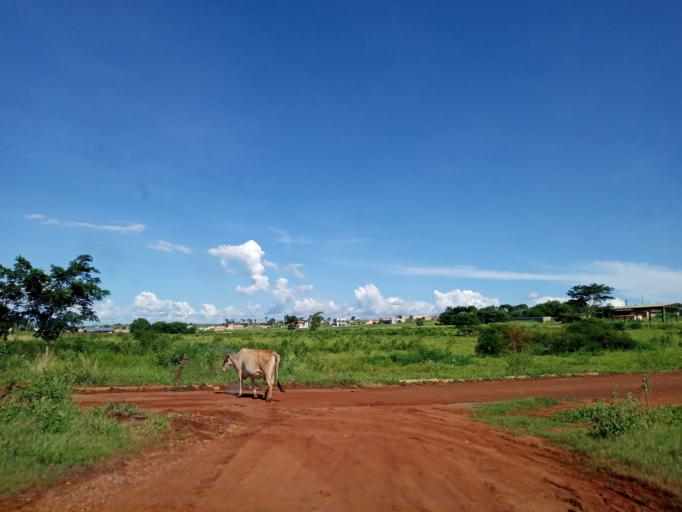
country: BR
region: Goias
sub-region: Itumbiara
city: Itumbiara
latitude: -18.4219
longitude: -49.1913
